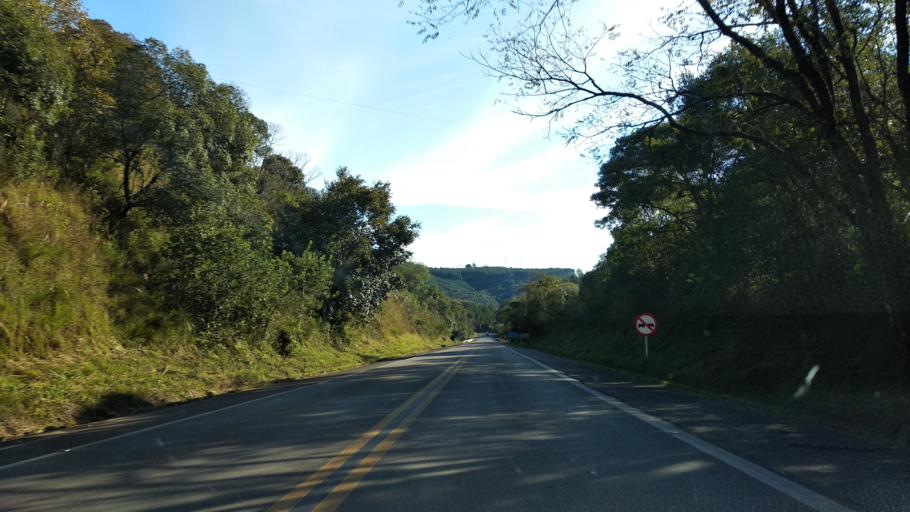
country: BR
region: Santa Catarina
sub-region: Celso Ramos
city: Celso Ramos
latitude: -27.5492
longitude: -51.4390
